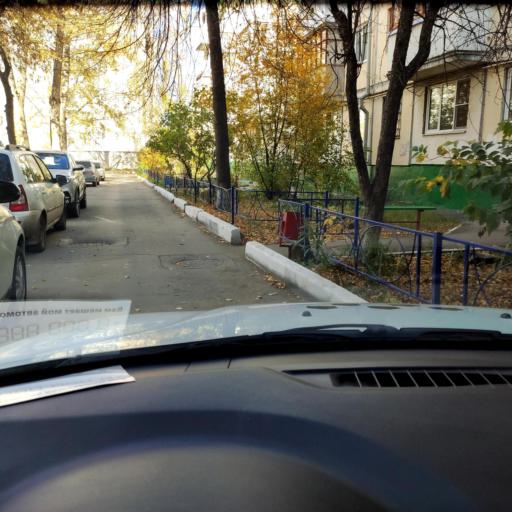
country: RU
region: Samara
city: Tol'yatti
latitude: 53.5113
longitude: 49.4315
